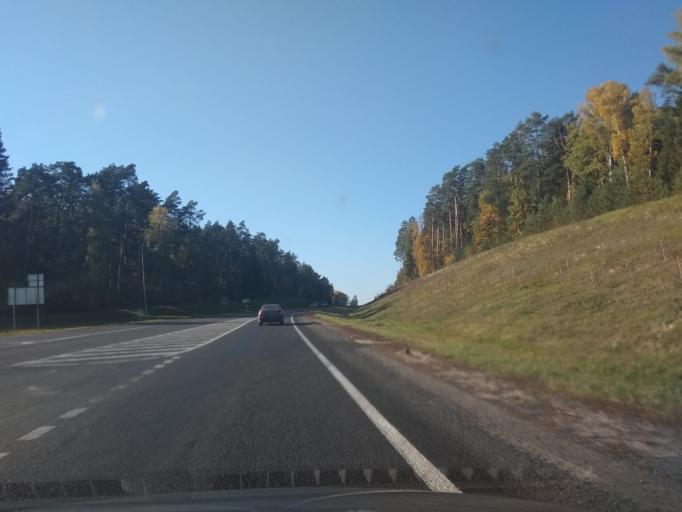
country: BY
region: Grodnenskaya
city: Zhyrovichy
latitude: 53.0468
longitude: 25.3548
